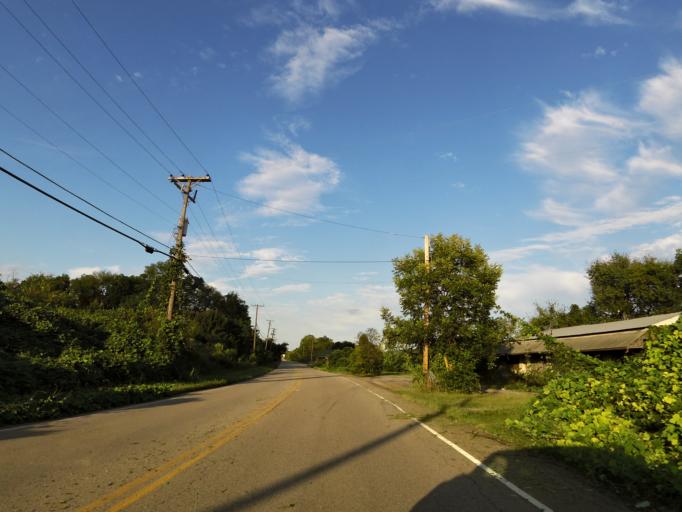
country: US
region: Tennessee
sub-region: Knox County
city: Knoxville
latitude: 36.0249
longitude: -83.8471
